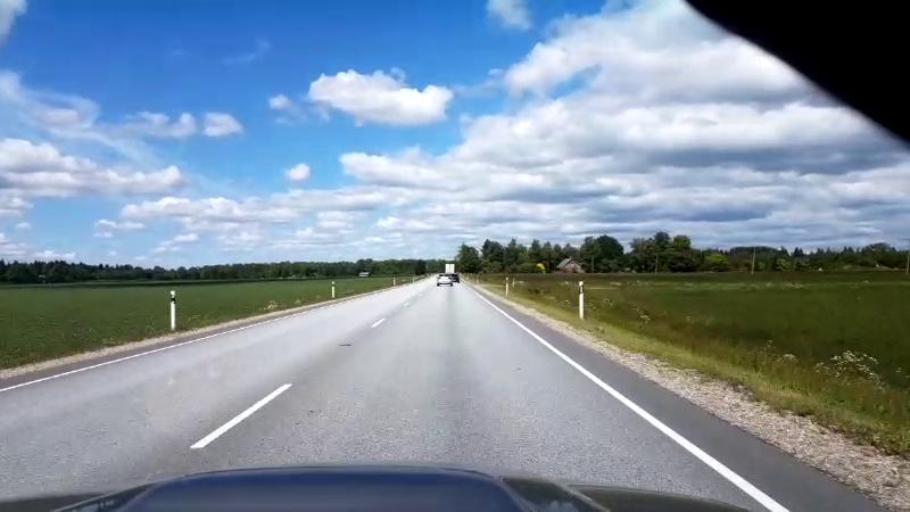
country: EE
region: Paernumaa
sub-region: Halinga vald
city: Parnu-Jaagupi
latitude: 58.5691
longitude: 24.5133
